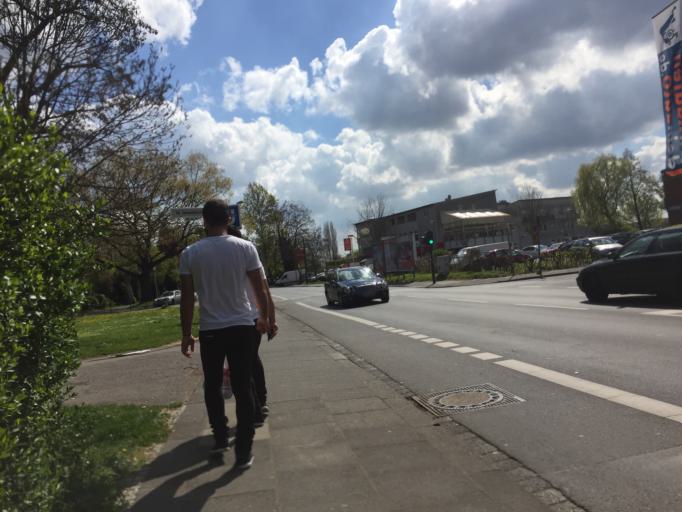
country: DE
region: North Rhine-Westphalia
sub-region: Regierungsbezirk Koln
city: Alfter
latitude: 50.7434
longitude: 7.0553
